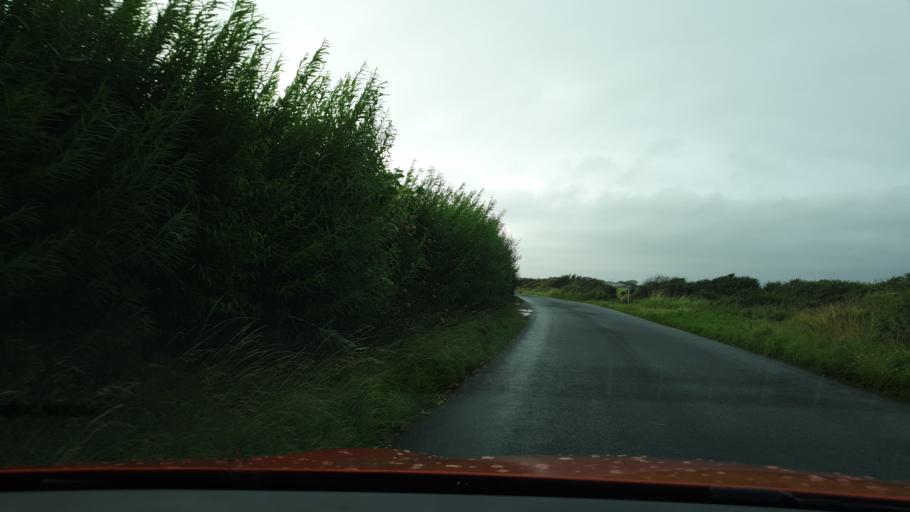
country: GB
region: England
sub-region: Cumbria
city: Barrow in Furness
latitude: 54.0799
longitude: -3.2321
